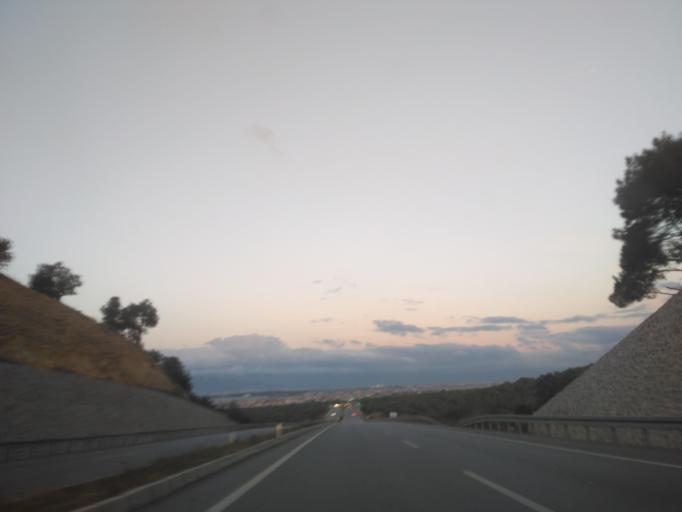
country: TR
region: Balikesir
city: Burhaniye
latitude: 39.4683
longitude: 26.9104
